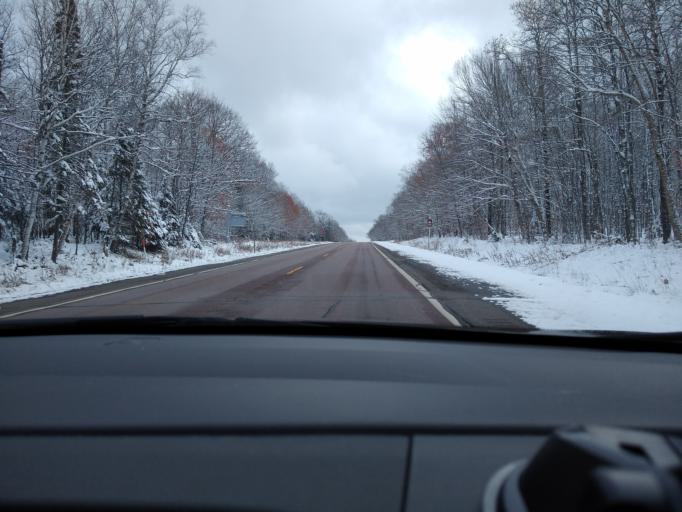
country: US
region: Wisconsin
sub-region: Vilas County
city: Eagle River
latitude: 46.2056
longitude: -89.0239
